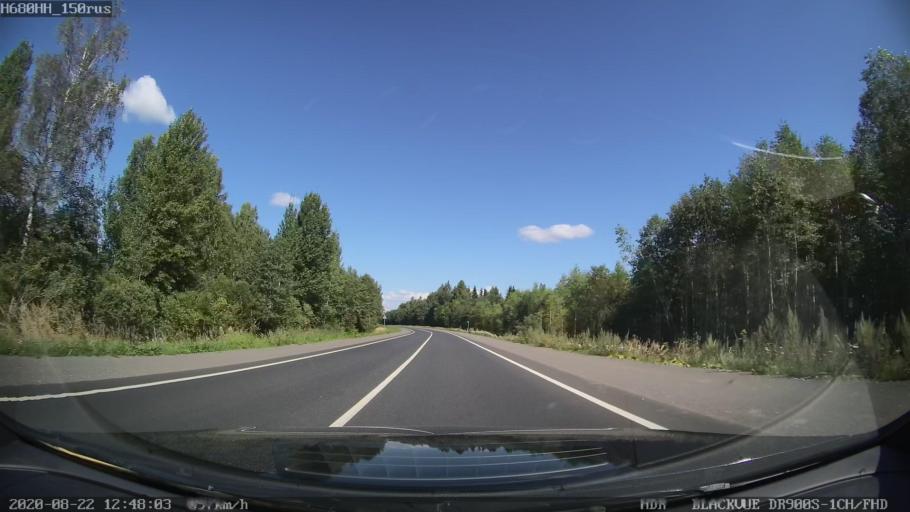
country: RU
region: Tverskaya
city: Rameshki
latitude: 57.4345
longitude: 36.1803
